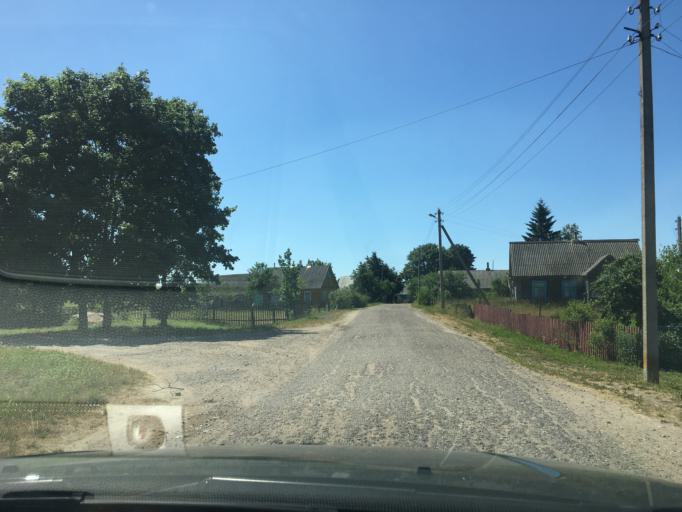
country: BY
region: Grodnenskaya
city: Hal'shany
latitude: 54.2586
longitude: 25.9884
